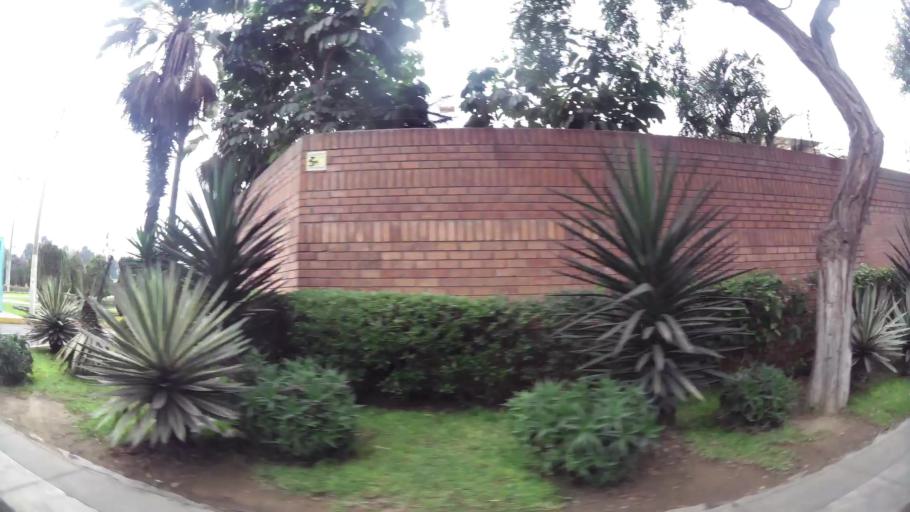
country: PE
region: Lima
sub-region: Lima
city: La Molina
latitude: -12.0778
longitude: -76.9180
